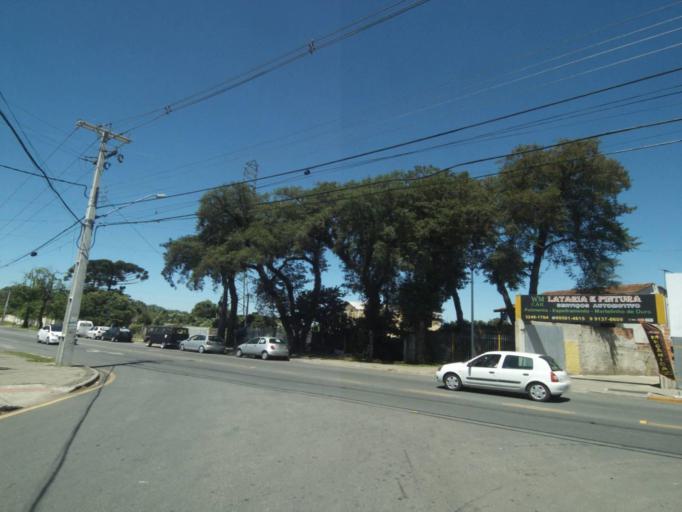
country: BR
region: Parana
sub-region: Curitiba
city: Curitiba
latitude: -25.4807
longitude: -49.3433
